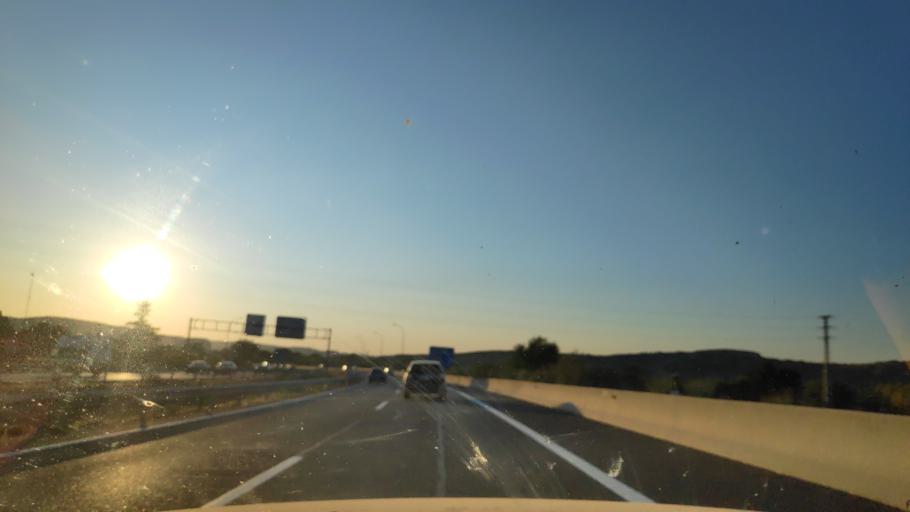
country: ES
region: Madrid
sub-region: Provincia de Madrid
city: Vaciamadrid
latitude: 40.3128
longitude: -3.4952
